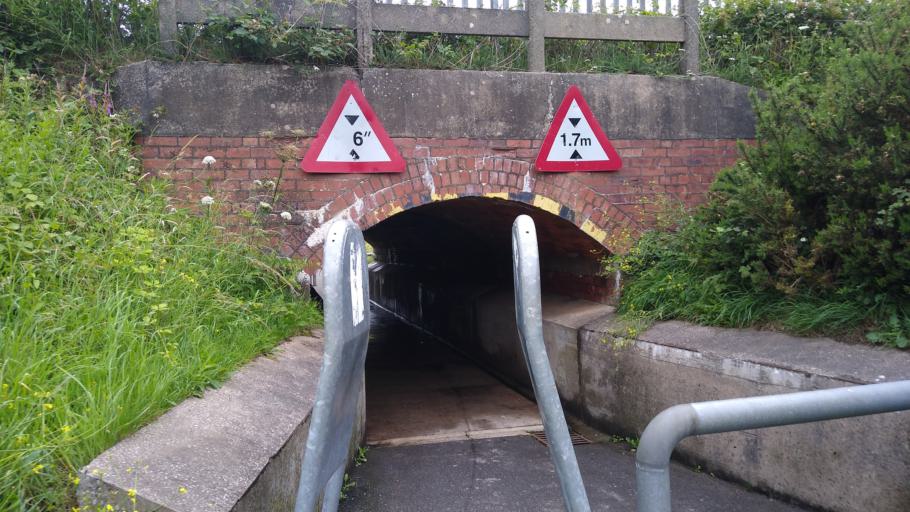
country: GB
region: England
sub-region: Cumbria
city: Flimby
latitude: 54.6978
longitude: -3.5142
